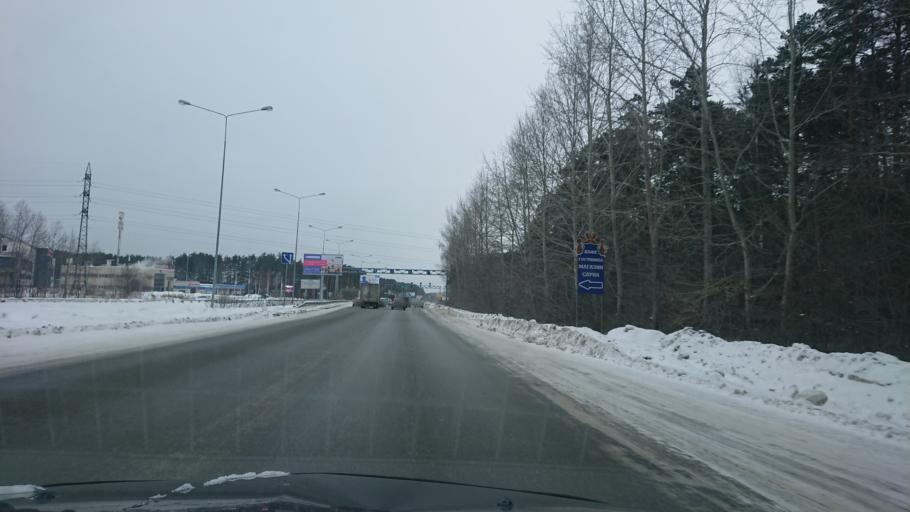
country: RU
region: Sverdlovsk
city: Shirokaya Rechka
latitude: 56.8115
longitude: 60.5209
